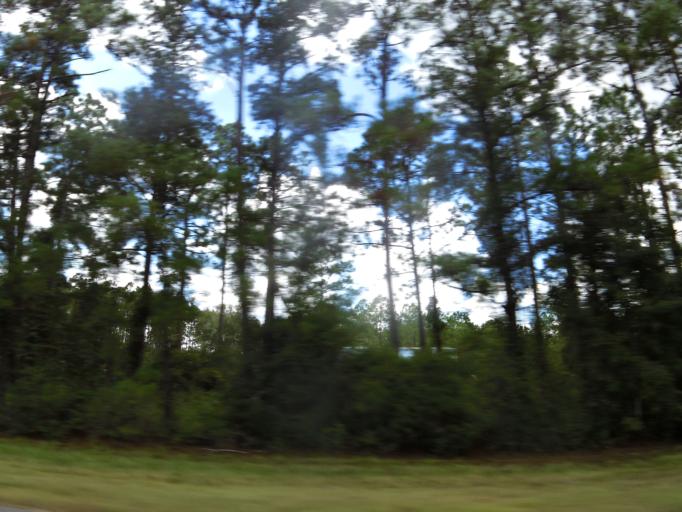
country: US
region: Georgia
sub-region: Charlton County
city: Folkston
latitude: 30.8873
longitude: -82.0153
